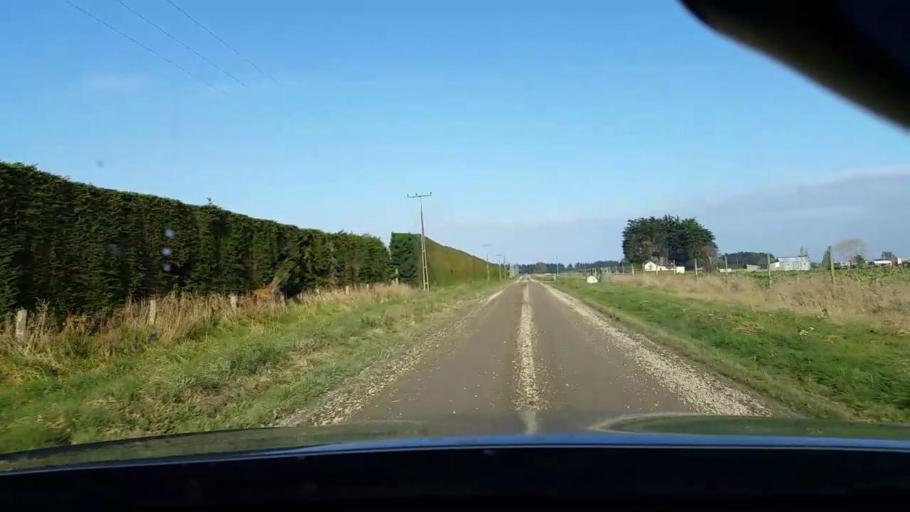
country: NZ
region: Southland
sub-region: Invercargill City
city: Invercargill
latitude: -46.2878
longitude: 168.2947
